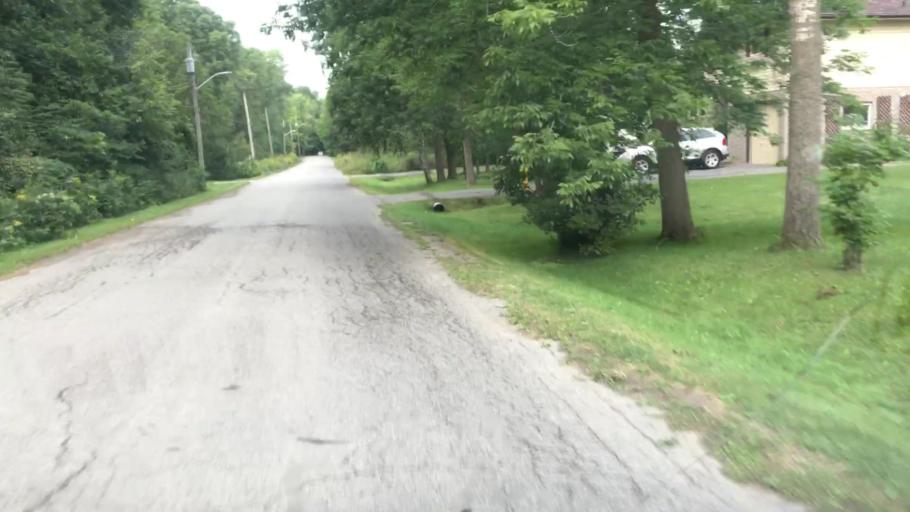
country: CA
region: Ontario
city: Quinte West
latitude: 44.0207
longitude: -77.7428
